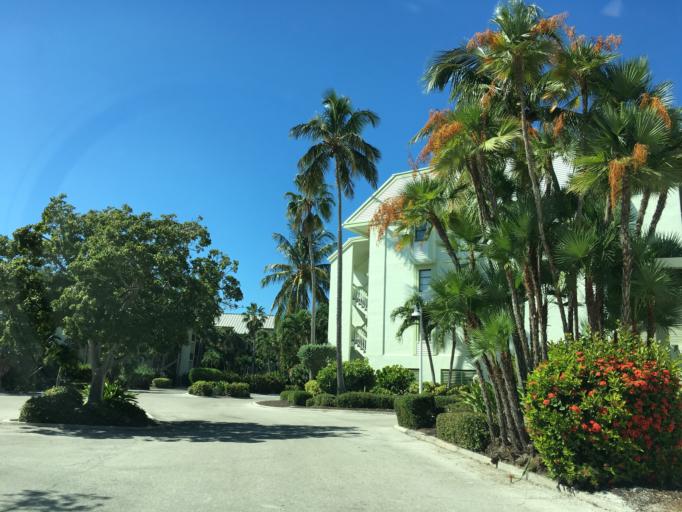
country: US
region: Florida
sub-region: Lee County
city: Pine Island Center
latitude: 26.5270
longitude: -82.1898
